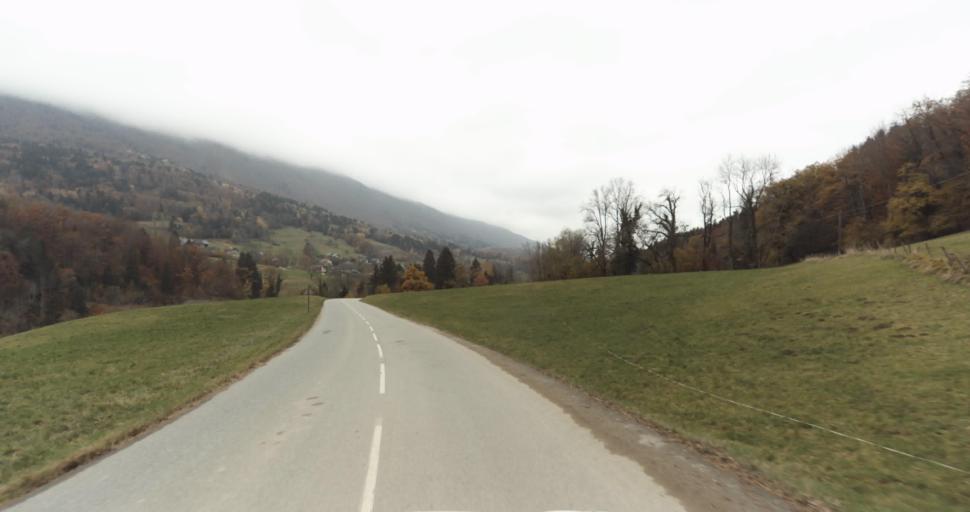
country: FR
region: Rhone-Alpes
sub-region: Departement de la Haute-Savoie
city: Saint-Jorioz
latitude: 45.8047
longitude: 6.1470
